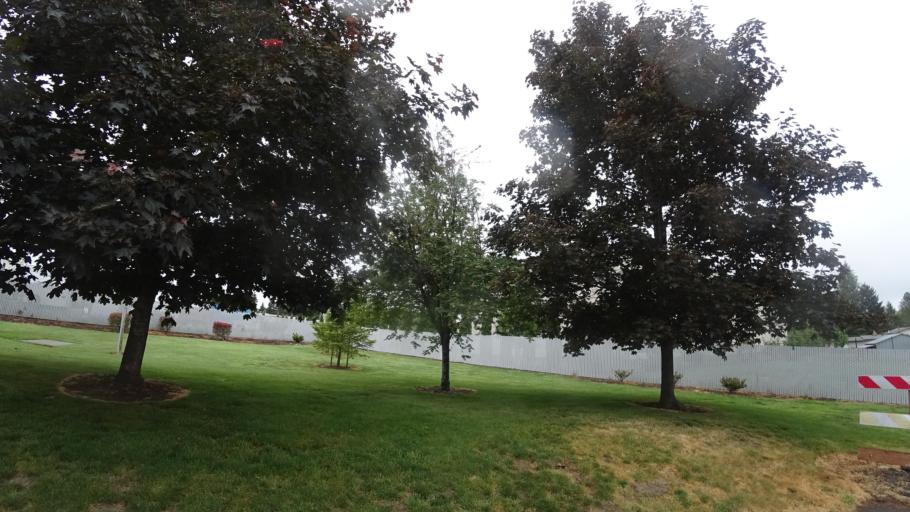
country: US
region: Oregon
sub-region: Washington County
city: Rockcreek
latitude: 45.5355
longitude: -122.8945
